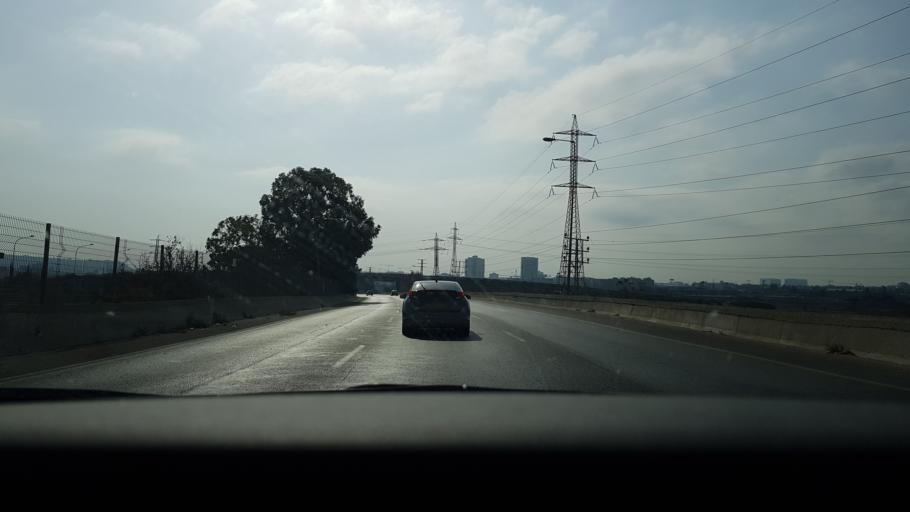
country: IL
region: Tel Aviv
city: Azor
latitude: 32.0404
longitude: 34.7901
